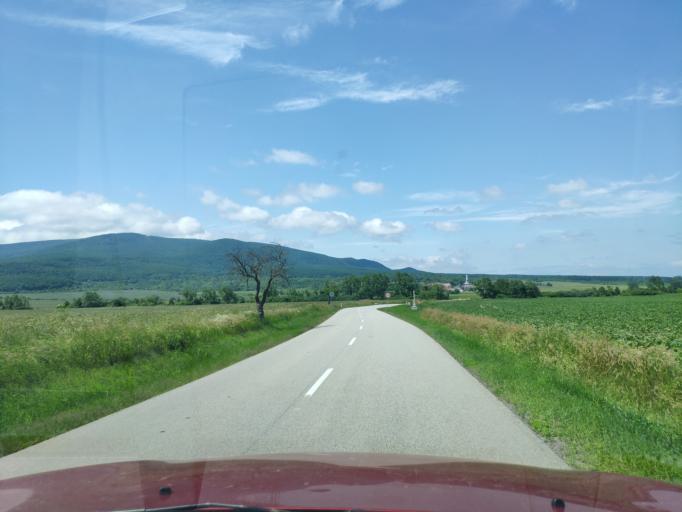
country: SK
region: Kosicky
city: Secovce
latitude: 48.7470
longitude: 21.6442
